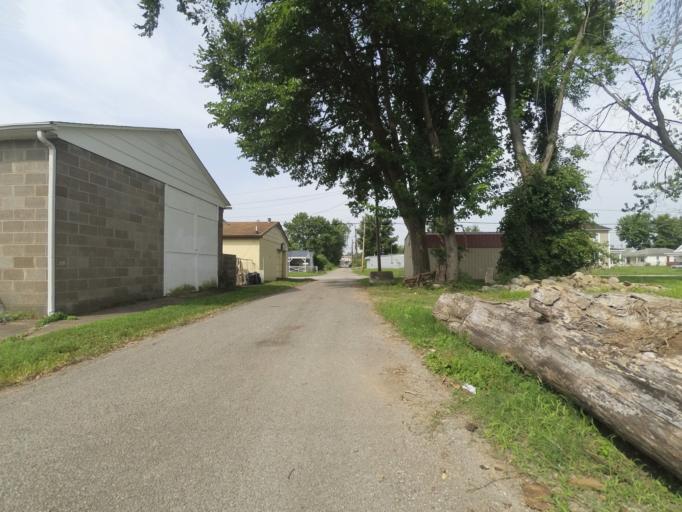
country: US
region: West Virginia
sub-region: Cabell County
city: Huntington
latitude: 38.4083
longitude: -82.4761
